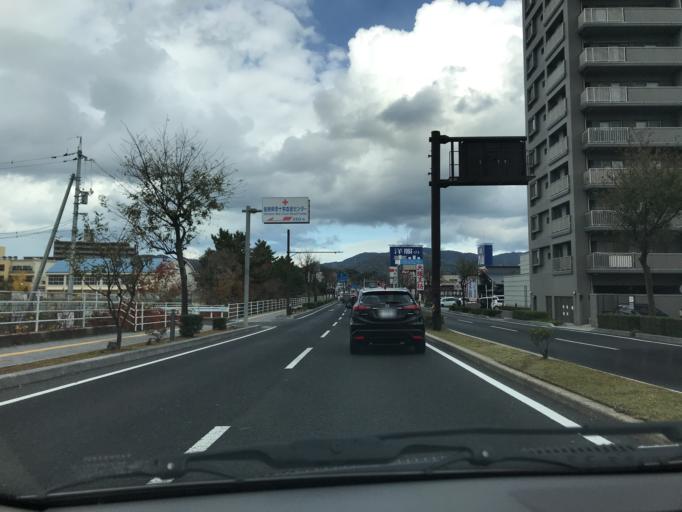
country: JP
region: Shimane
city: Matsue-shi
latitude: 35.4782
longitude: 133.0636
